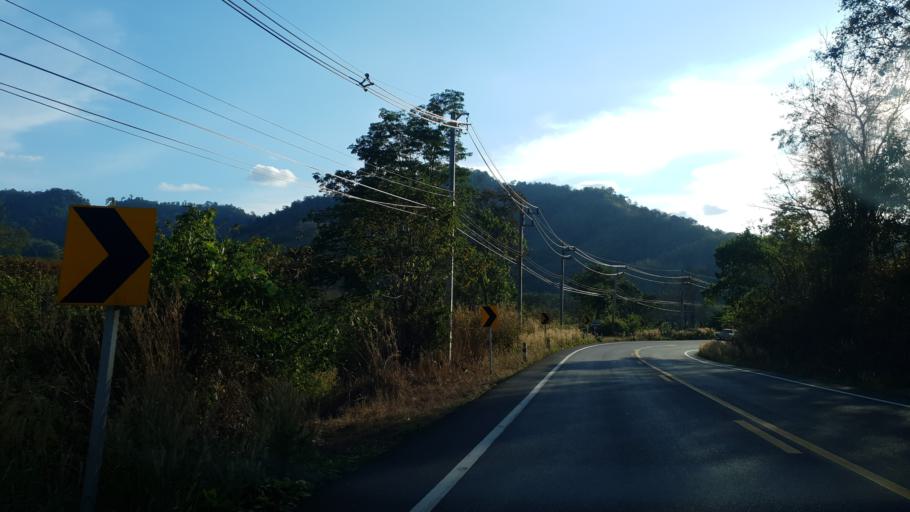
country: TH
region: Loei
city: Dan Sai
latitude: 17.2257
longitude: 101.0724
